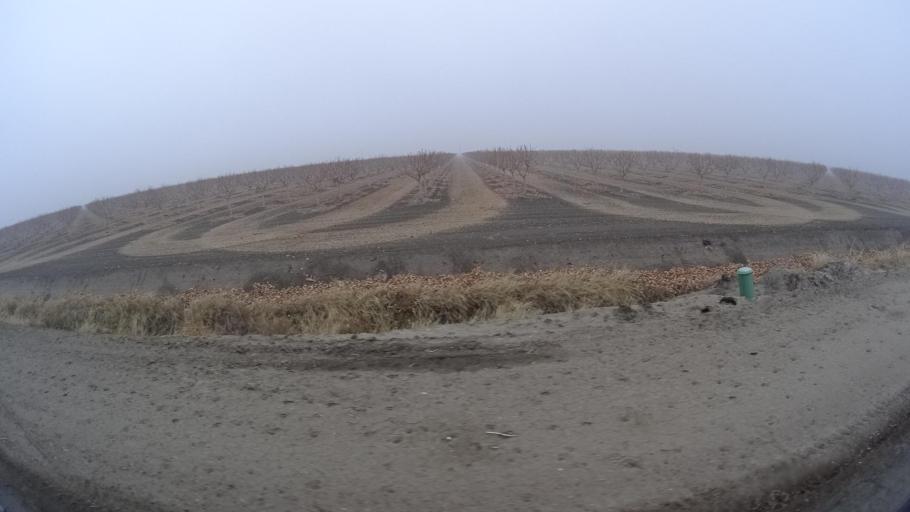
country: US
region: California
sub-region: Kern County
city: Buttonwillow
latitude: 35.4562
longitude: -119.5599
